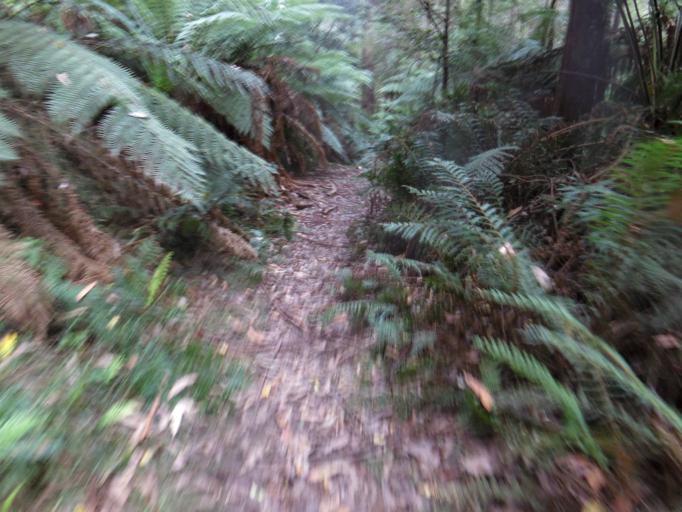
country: AU
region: Victoria
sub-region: Yarra Ranges
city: Healesville
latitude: -37.5129
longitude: 145.5192
